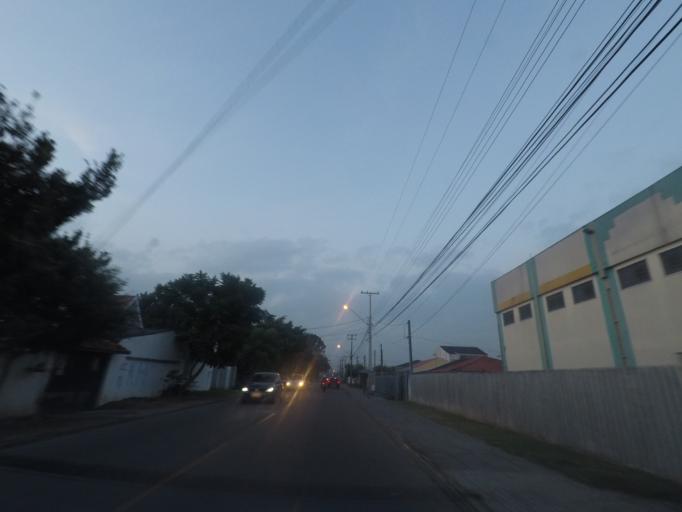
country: BR
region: Parana
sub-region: Pinhais
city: Pinhais
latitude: -25.4526
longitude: -49.1905
